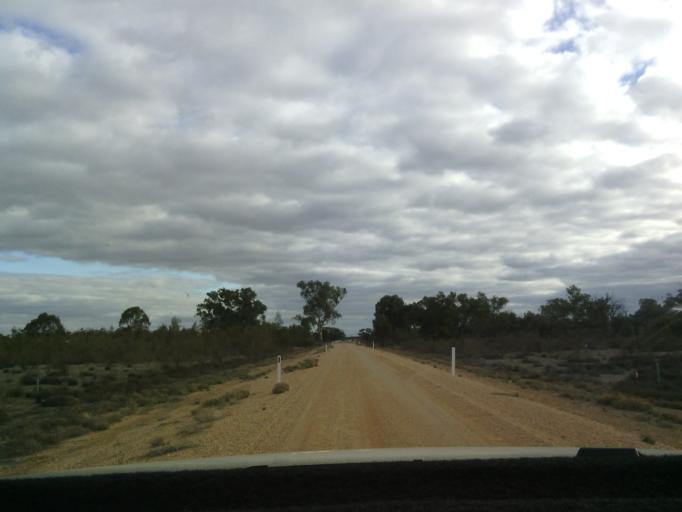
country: AU
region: South Australia
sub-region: Renmark Paringa
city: Renmark
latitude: -34.1669
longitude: 141.1868
